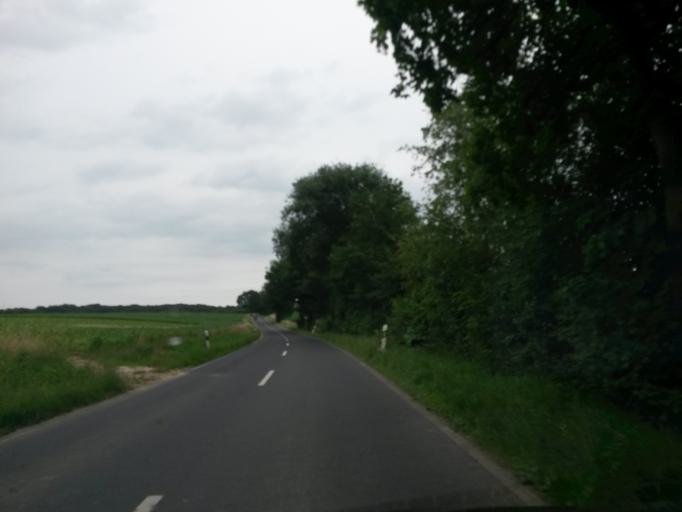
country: DE
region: North Rhine-Westphalia
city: Lohmar
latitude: 50.8535
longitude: 7.2862
